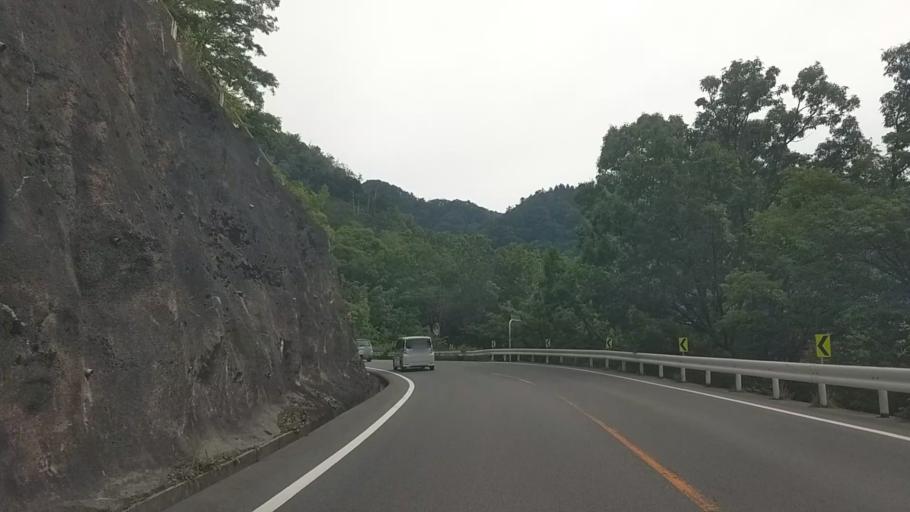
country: JP
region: Yamanashi
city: Isawa
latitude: 35.5659
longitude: 138.5935
